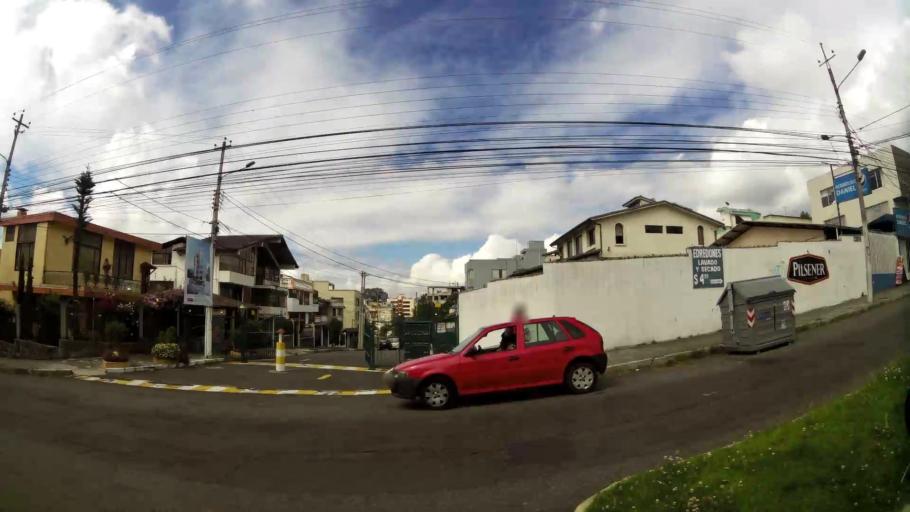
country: EC
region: Pichincha
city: Quito
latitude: -0.1558
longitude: -78.4931
